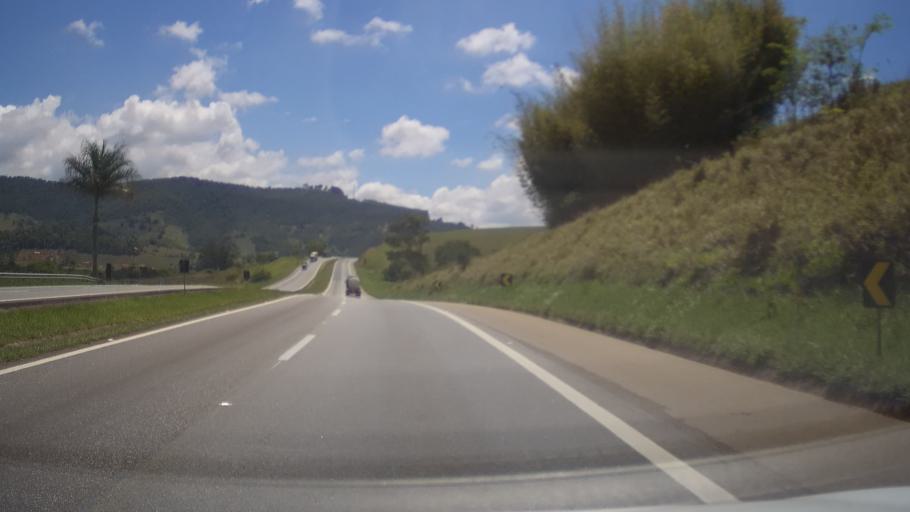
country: BR
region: Minas Gerais
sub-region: Campanha
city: Campanha
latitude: -21.8212
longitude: -45.4937
